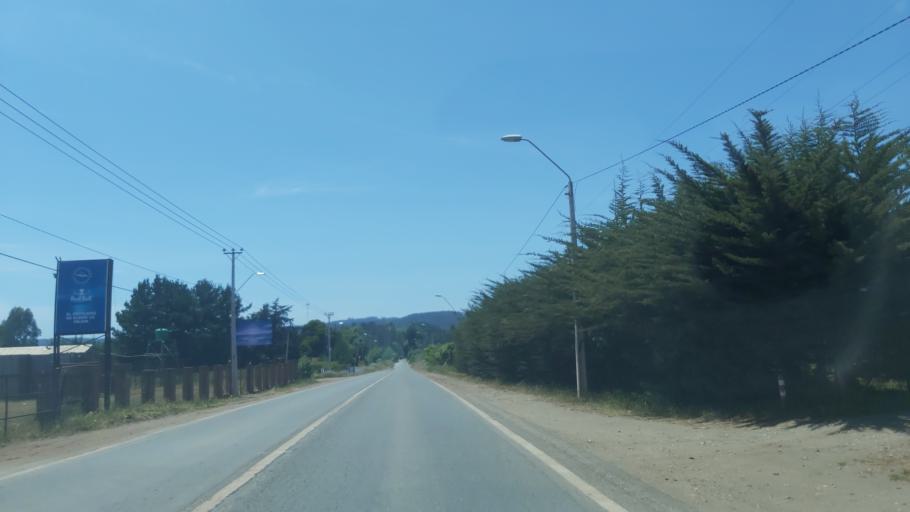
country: CL
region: Maule
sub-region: Provincia de Cauquenes
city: Cauquenes
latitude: -35.7955
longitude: -72.5501
